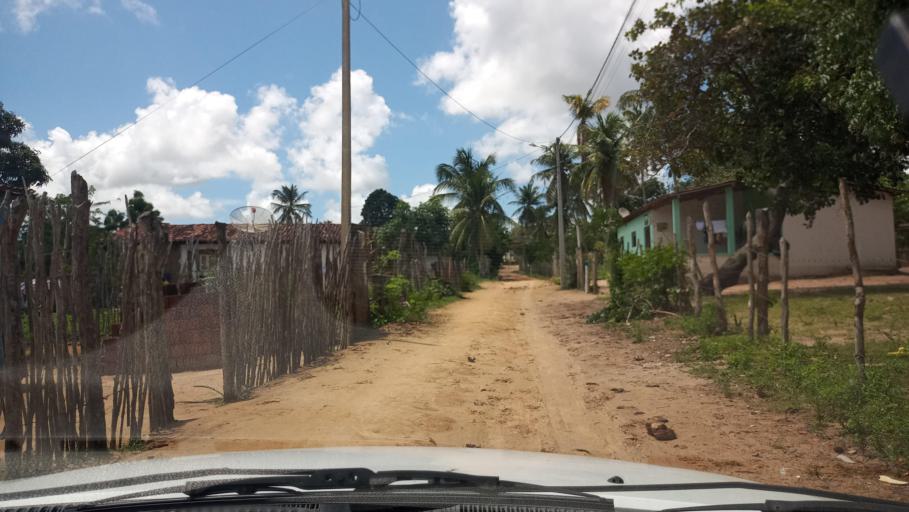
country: BR
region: Rio Grande do Norte
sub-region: Goianinha
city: Goianinha
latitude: -6.2990
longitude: -35.2204
